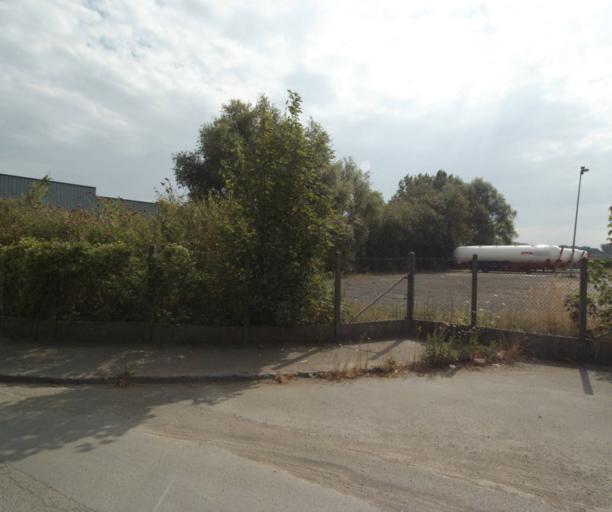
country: FR
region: Nord-Pas-de-Calais
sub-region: Departement du Nord
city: Santes
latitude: 50.5940
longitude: 2.9753
